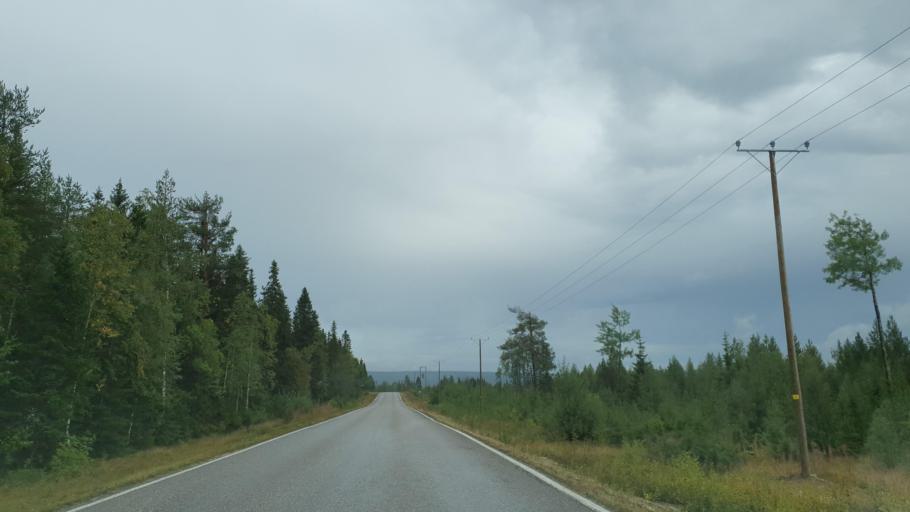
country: FI
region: Kainuu
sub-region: Kajaani
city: Paltamo
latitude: 64.6606
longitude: 27.8761
